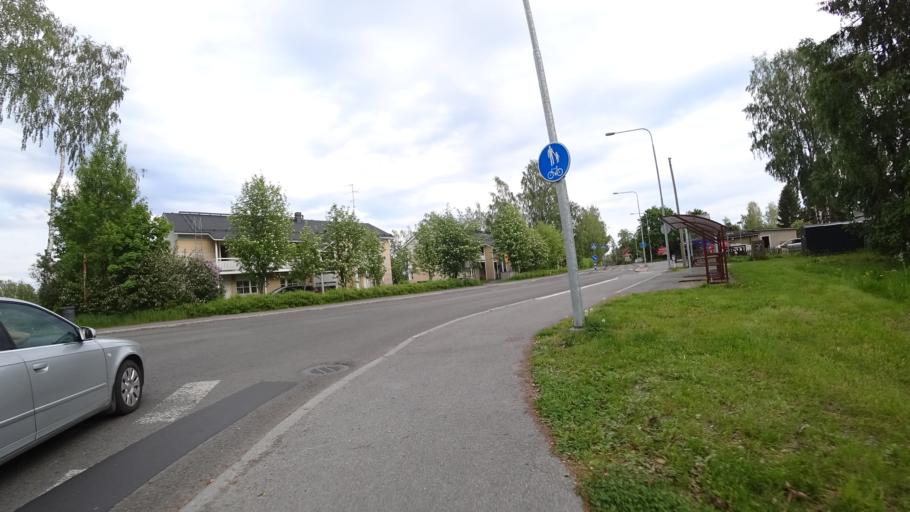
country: FI
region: Pirkanmaa
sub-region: Tampere
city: Yloejaervi
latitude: 61.5232
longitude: 23.6353
